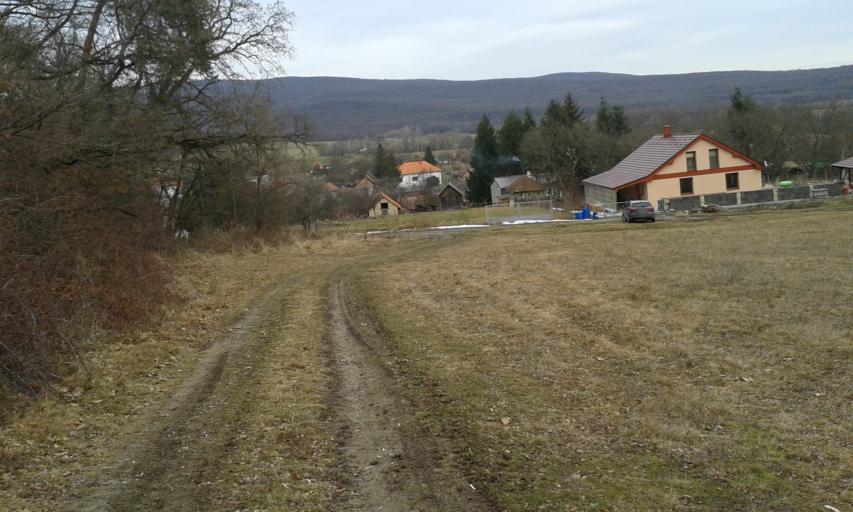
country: SK
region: Nitriansky
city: Zlate Moravce
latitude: 48.4632
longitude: 18.3095
